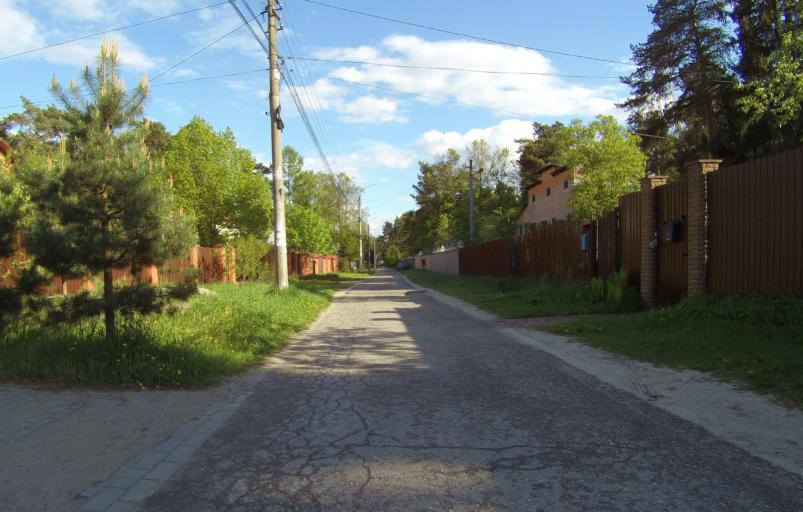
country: RU
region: Moskovskaya
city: Kratovo
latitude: 55.5931
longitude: 38.1674
